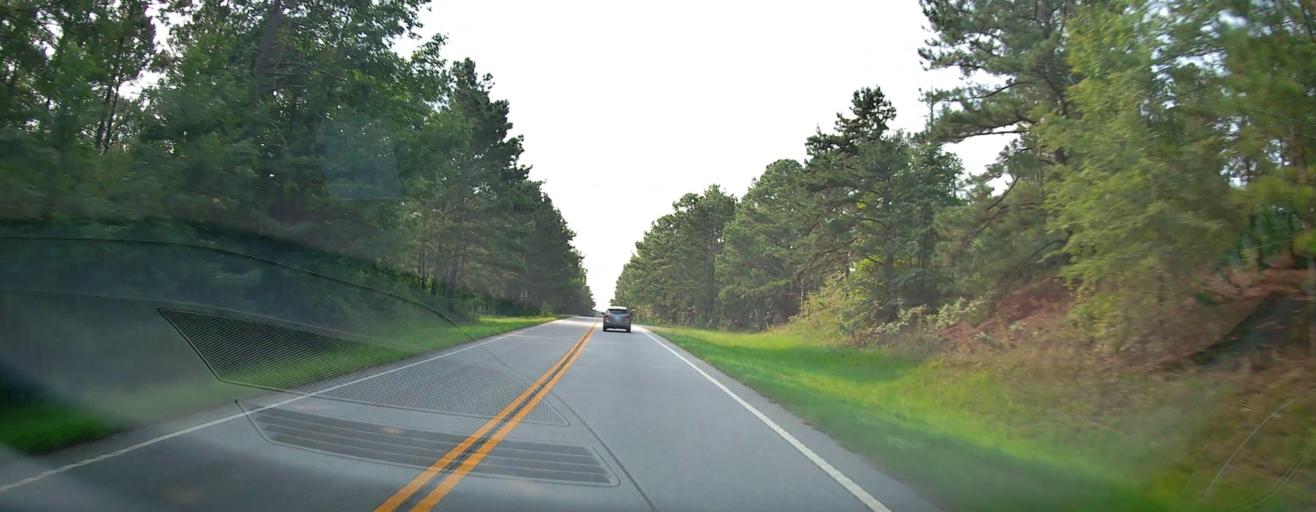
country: US
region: Georgia
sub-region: Monroe County
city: Forsyth
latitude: 33.0327
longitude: -83.7475
